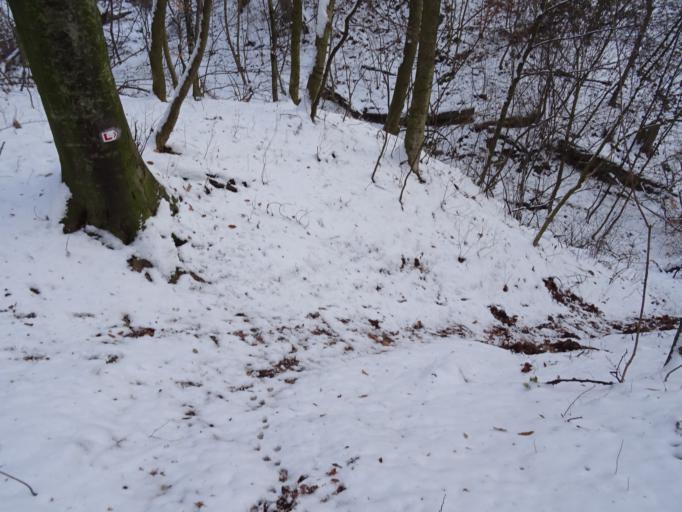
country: HU
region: Fejer
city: Mor
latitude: 47.3786
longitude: 18.2441
